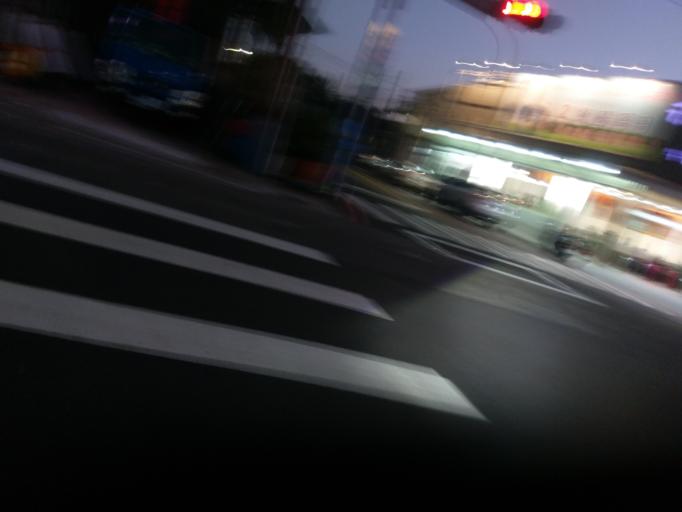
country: TW
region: Taiwan
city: Taoyuan City
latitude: 25.0439
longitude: 121.1385
